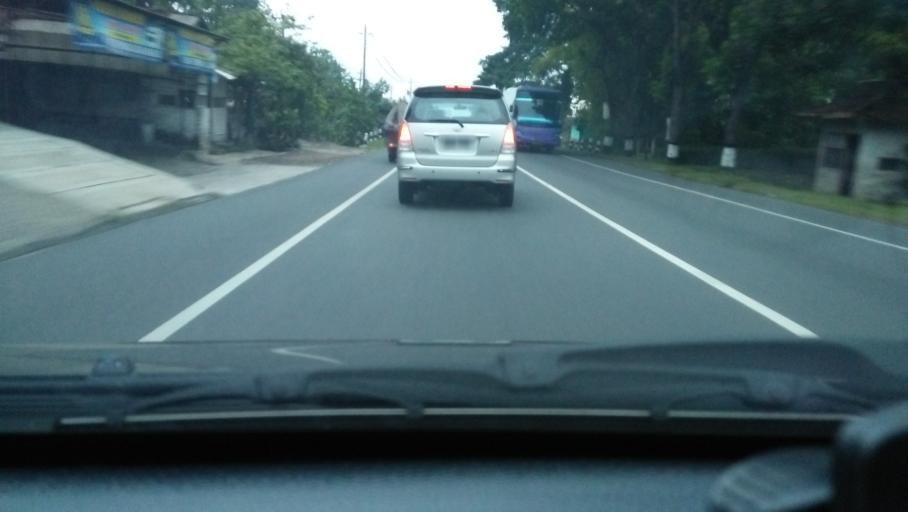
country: ID
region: Central Java
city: Magelang
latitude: -7.4077
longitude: 110.2382
